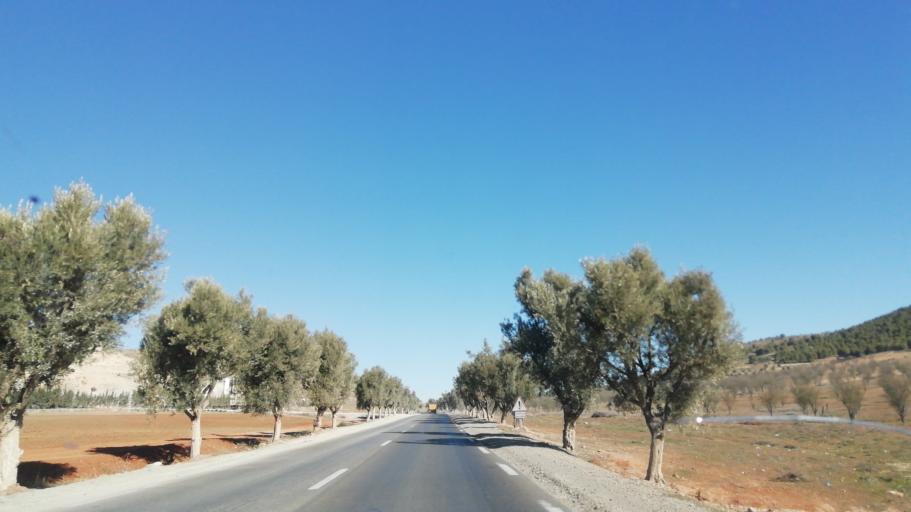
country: DZ
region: Mascara
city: Mascara
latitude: 35.2374
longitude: 0.1172
